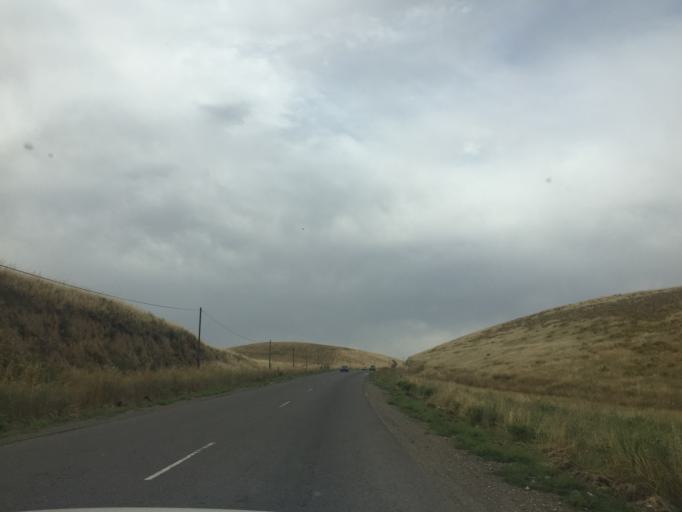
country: TJ
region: Khatlon
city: Danghara
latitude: 37.9799
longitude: 69.3414
